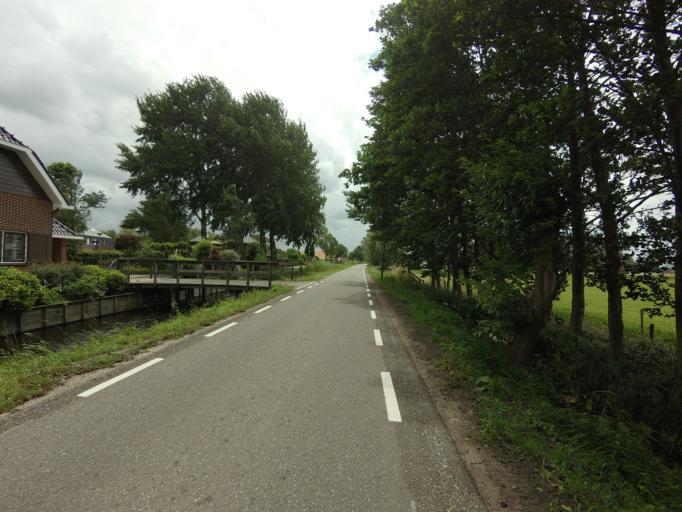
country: NL
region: North Holland
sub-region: Gemeente Wijdemeren
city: Kortenhoef
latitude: 52.2455
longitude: 5.1124
